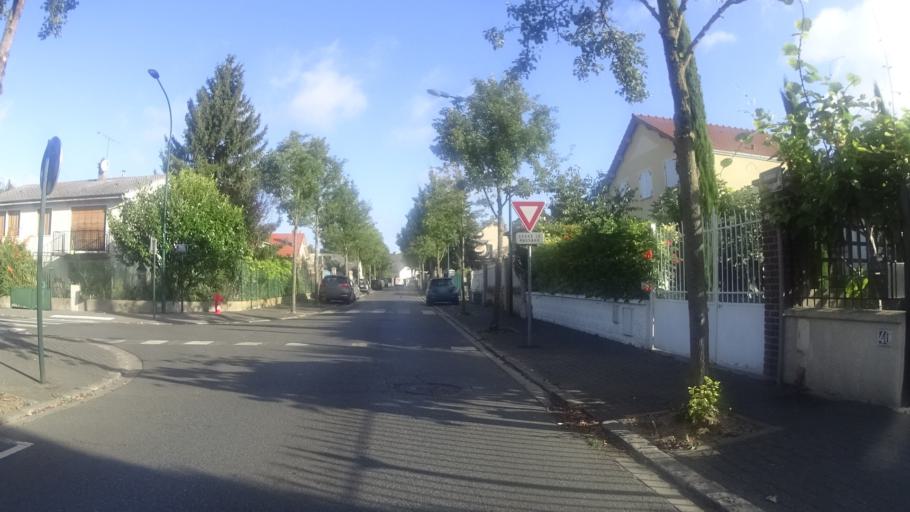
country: FR
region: Ile-de-France
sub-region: Departement de l'Essonne
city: Viry-Chatillon
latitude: 48.6831
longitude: 2.3982
